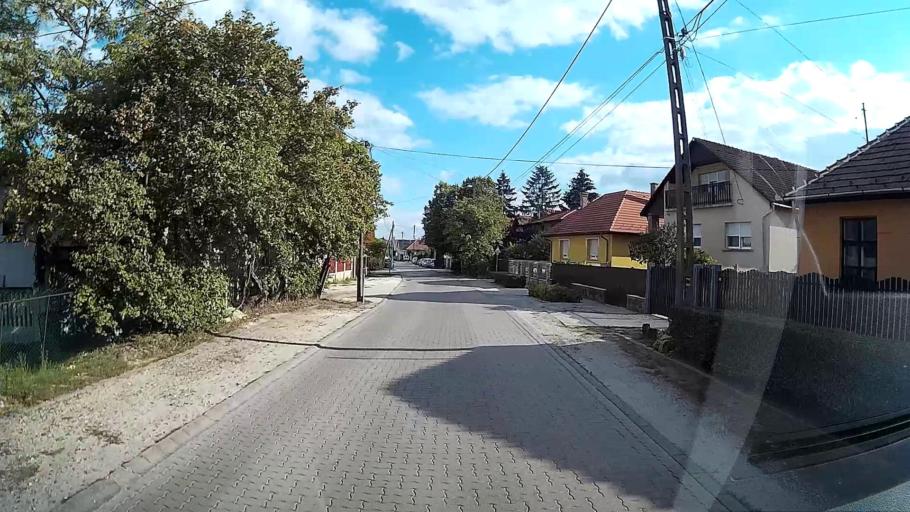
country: HU
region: Pest
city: Pilisvorosvar
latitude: 47.6255
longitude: 18.9009
